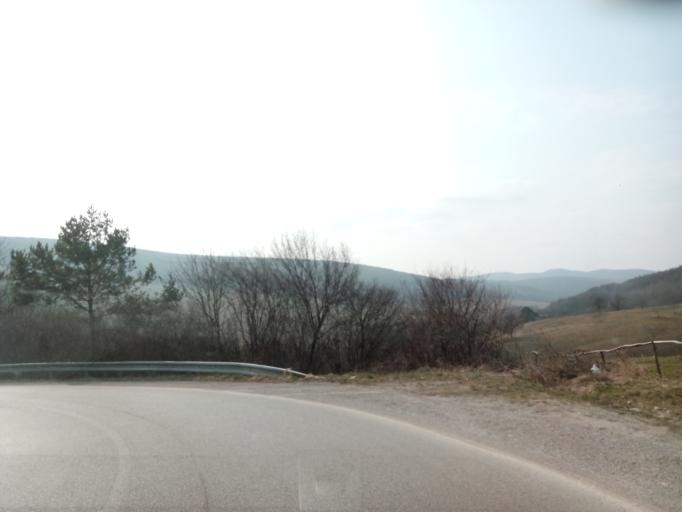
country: SK
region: Trenciansky
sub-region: Okres Trencin
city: Trencin
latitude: 48.9243
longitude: 18.0371
